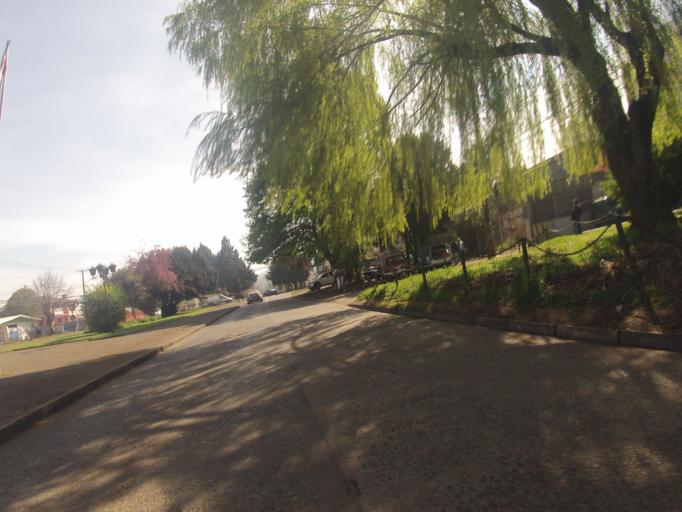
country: CL
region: Araucania
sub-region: Provincia de Cautin
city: Temuco
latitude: -38.7353
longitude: -72.6007
